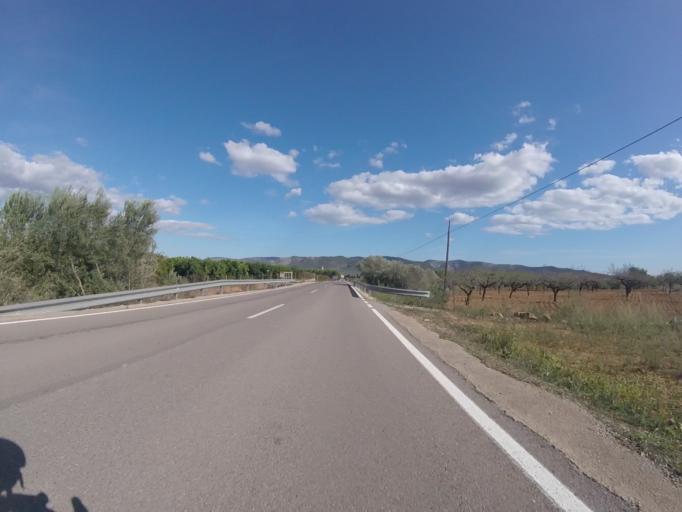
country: ES
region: Valencia
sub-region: Provincia de Castello
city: Alcala de Xivert
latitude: 40.3026
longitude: 0.2062
